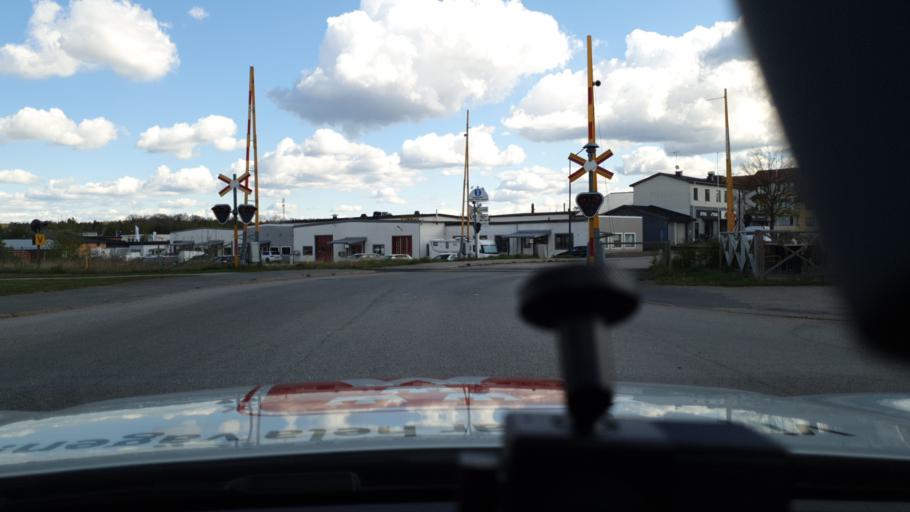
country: SE
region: Kalmar
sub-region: Vimmerby Kommun
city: Vimmerby
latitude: 57.6660
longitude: 15.8453
